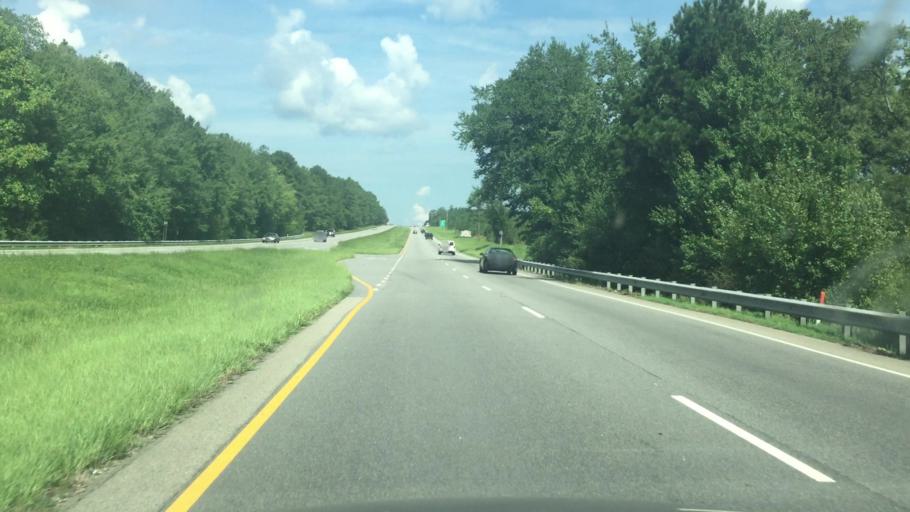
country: US
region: North Carolina
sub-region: Richmond County
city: Hamlet
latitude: 34.8569
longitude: -79.6265
